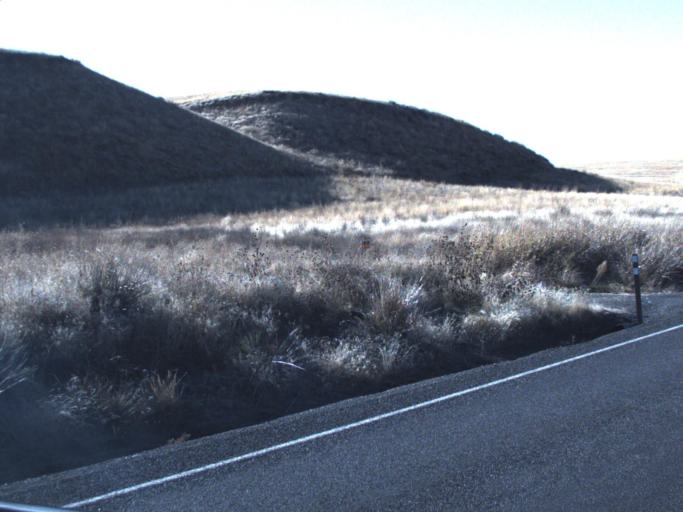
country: US
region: Washington
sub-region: Adams County
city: Ritzville
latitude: 46.8200
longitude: -118.3166
